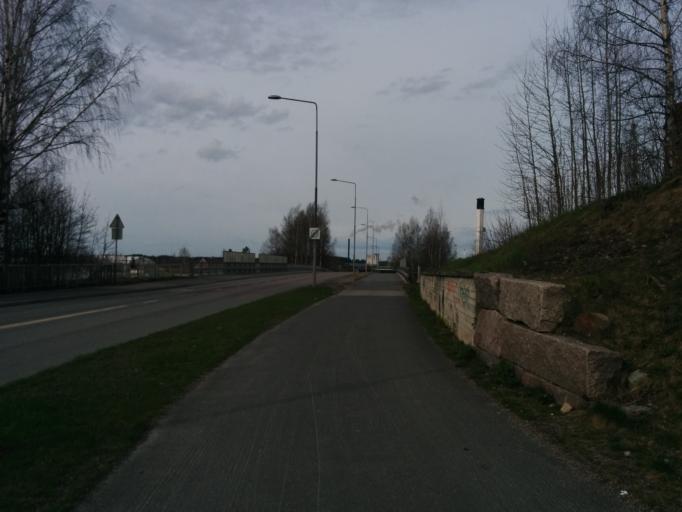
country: FI
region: Haeme
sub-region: Riihimaeki
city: Riihimaeki
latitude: 60.7305
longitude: 24.7875
